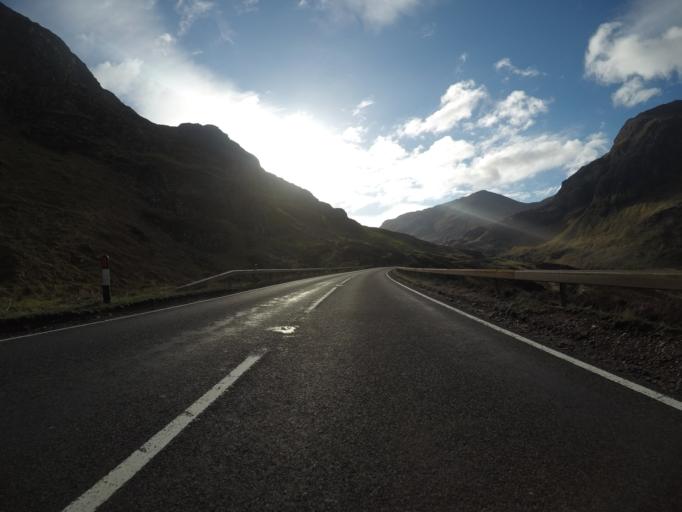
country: GB
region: Scotland
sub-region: Highland
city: Fort William
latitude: 56.6677
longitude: -4.9851
